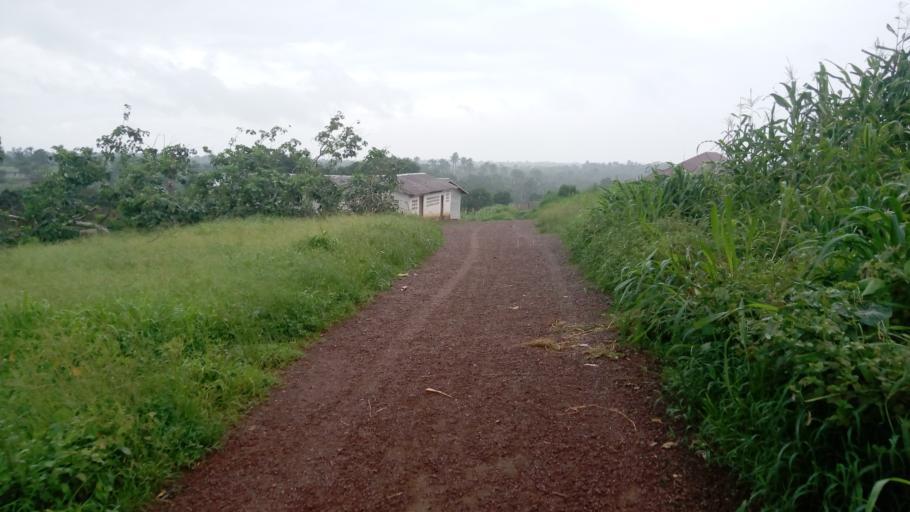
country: SL
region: Southern Province
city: Rotifunk
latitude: 8.4835
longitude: -12.7591
